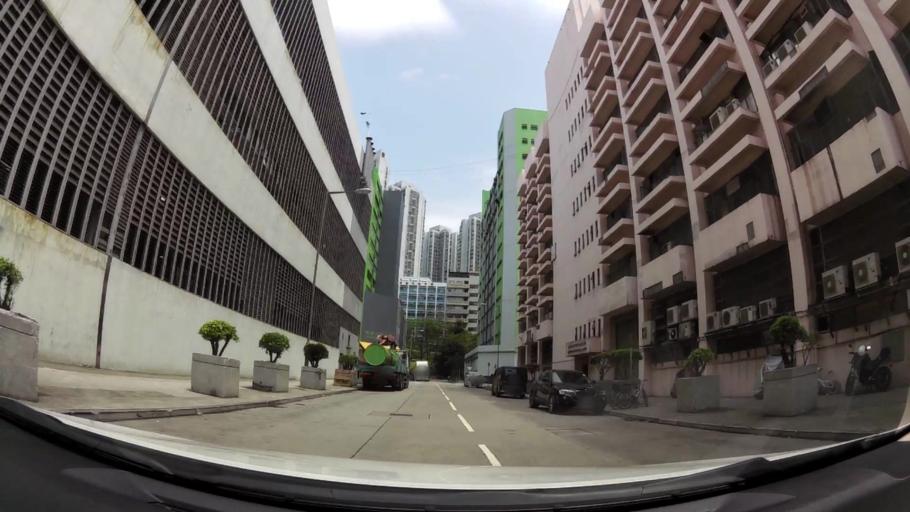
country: HK
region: Tuen Mun
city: Tuen Mun
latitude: 22.3970
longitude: 113.9711
